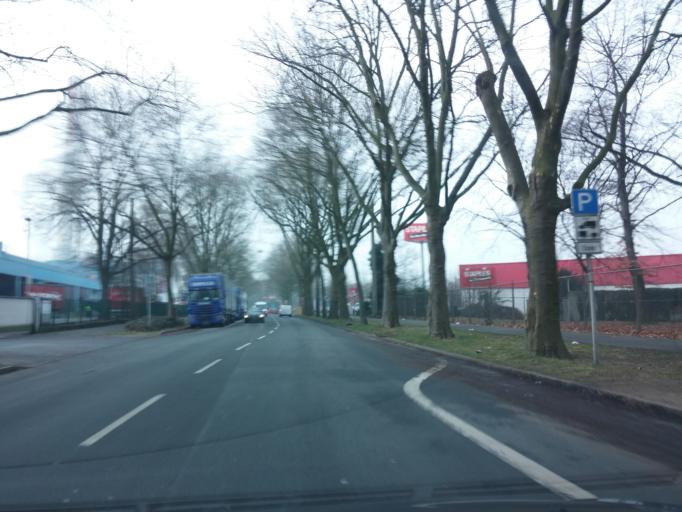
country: DE
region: North Rhine-Westphalia
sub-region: Regierungsbezirk Munster
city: Gladbeck
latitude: 51.5669
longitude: 6.9681
